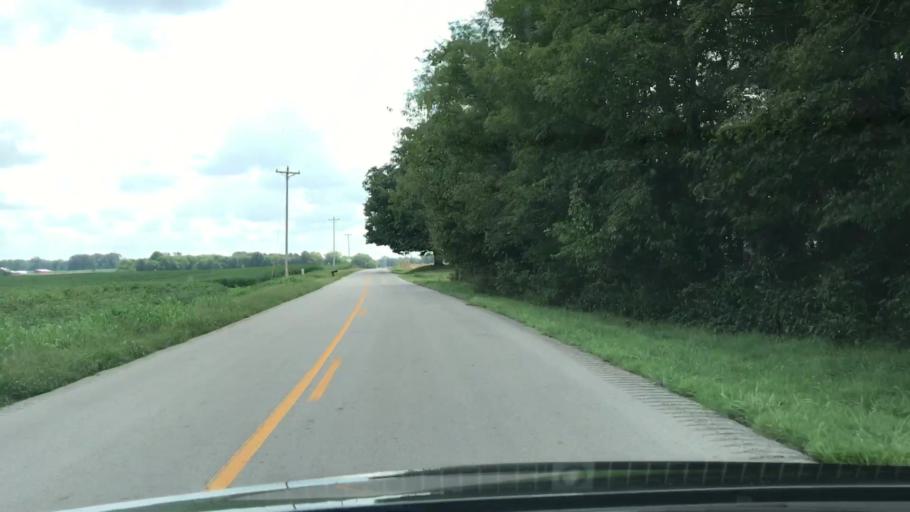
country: US
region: Kentucky
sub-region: Todd County
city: Elkton
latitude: 36.7712
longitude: -87.1165
